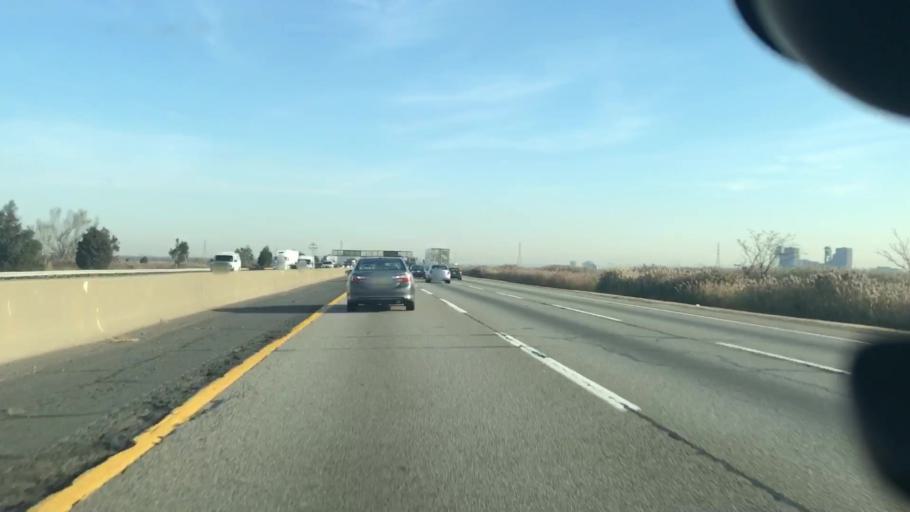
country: US
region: New Jersey
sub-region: Bergen County
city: North Arlington
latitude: 40.7712
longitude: -74.1057
